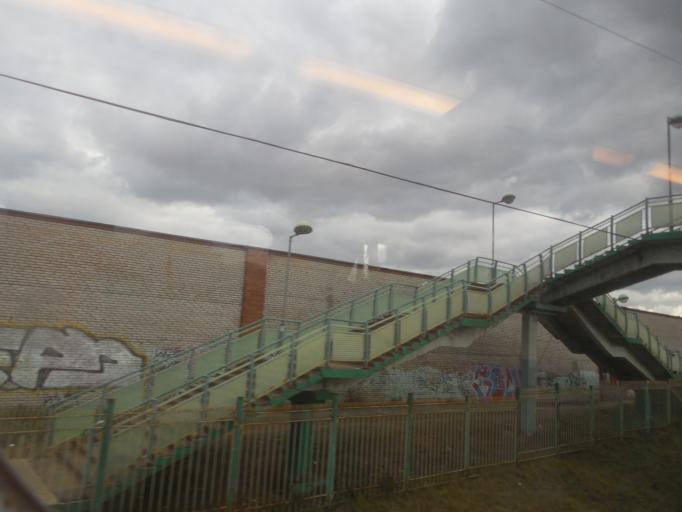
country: RU
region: Moskovskaya
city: Tomilino
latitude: 55.6689
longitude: 37.9246
